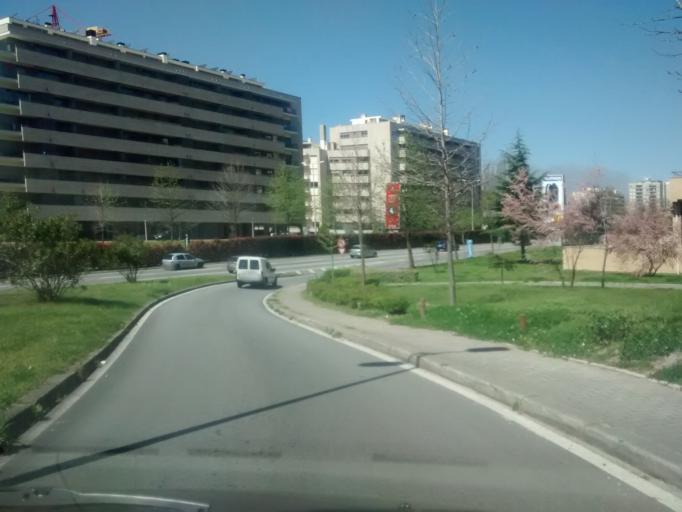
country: PT
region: Braga
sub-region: Braga
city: Braga
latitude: 41.5485
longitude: -8.4049
